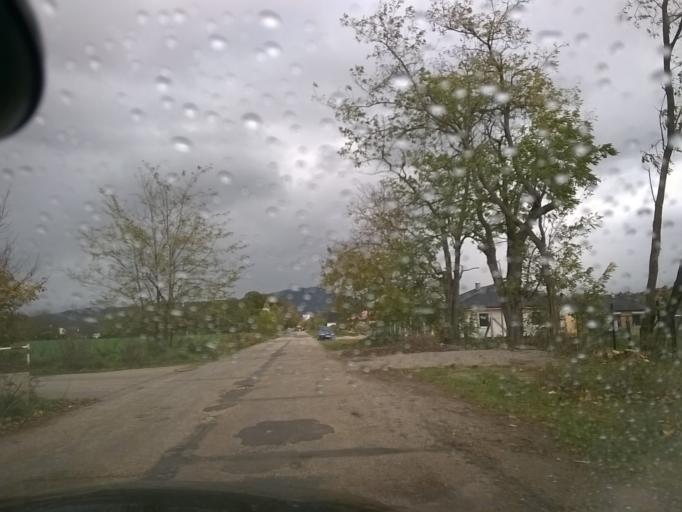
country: SK
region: Nitriansky
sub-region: Okres Nitra
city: Nitra
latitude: 48.3126
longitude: 18.0315
